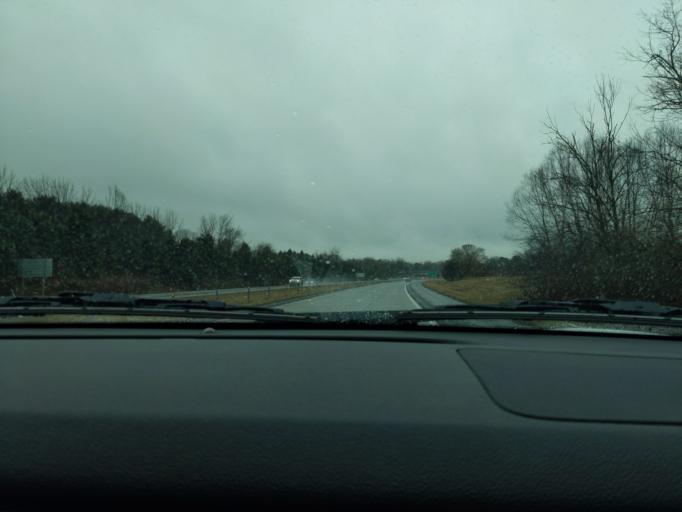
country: US
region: Pennsylvania
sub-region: Bucks County
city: Doylestown
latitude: 40.3097
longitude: -75.1490
